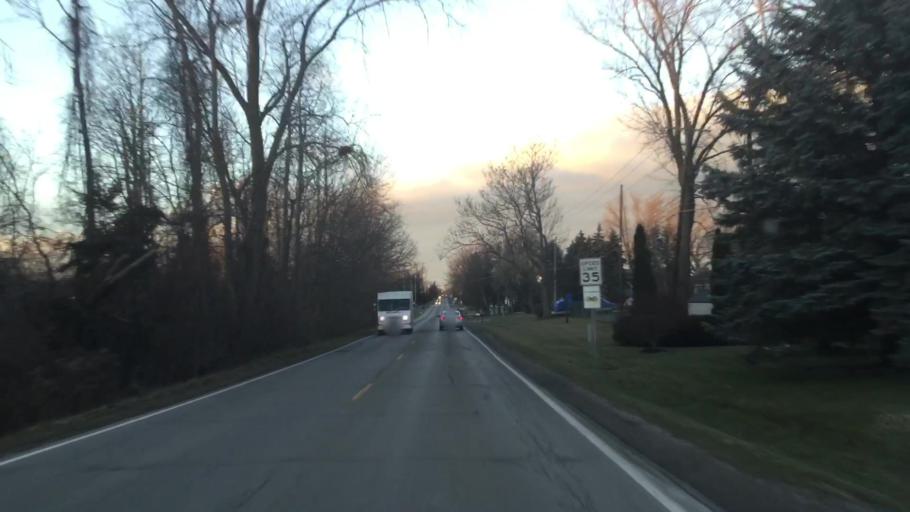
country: US
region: Michigan
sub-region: Genesee County
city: Lake Fenton
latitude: 42.8516
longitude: -83.7290
